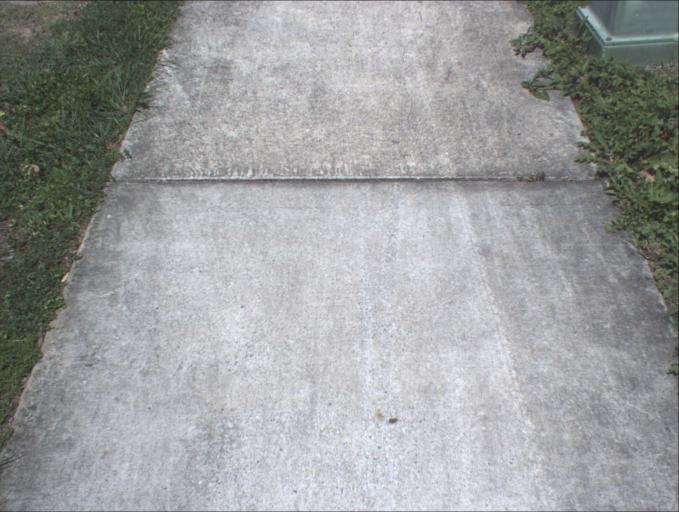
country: AU
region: Queensland
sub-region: Logan
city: Waterford West
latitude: -27.7166
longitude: 153.1495
